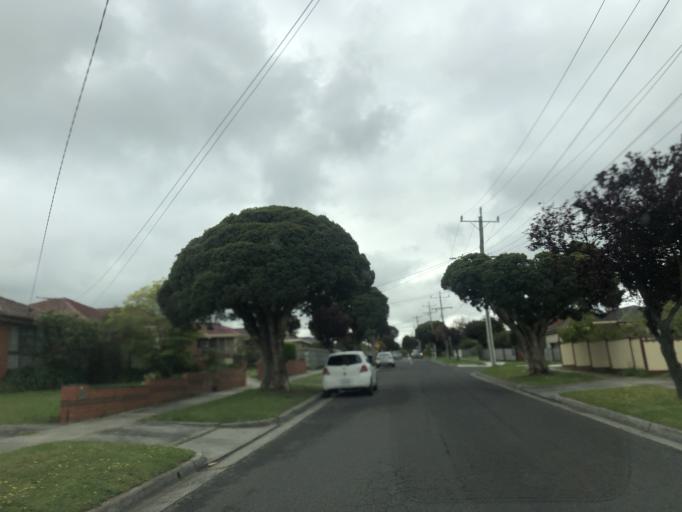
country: AU
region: Victoria
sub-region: Greater Dandenong
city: Dandenong North
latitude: -37.9592
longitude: 145.2149
